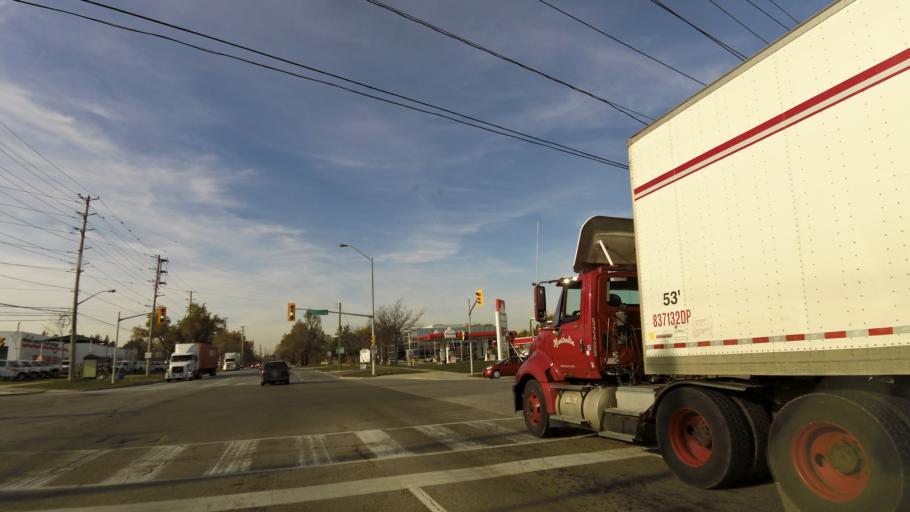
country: CA
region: Ontario
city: Brampton
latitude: 43.7169
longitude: -79.6835
